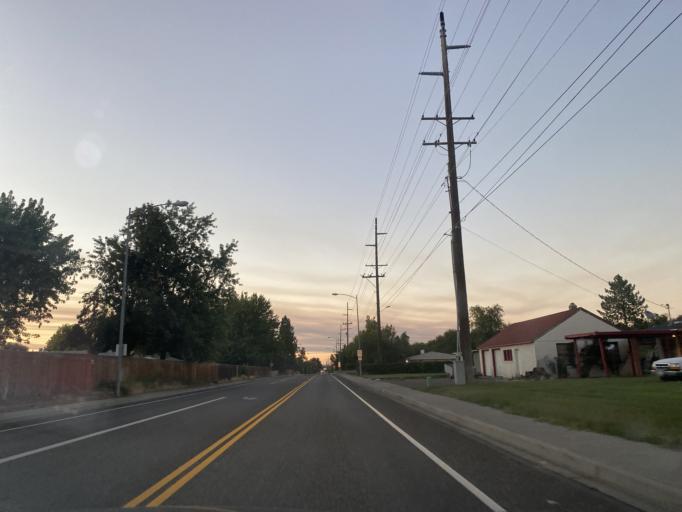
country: US
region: Washington
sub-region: Benton County
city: Kennewick
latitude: 46.1994
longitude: -119.1696
